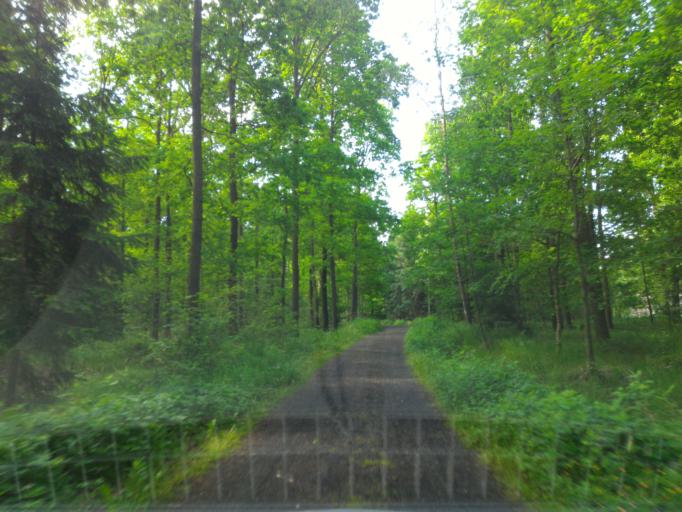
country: DE
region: Saxony
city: Grossschonau
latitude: 50.8752
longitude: 14.6655
